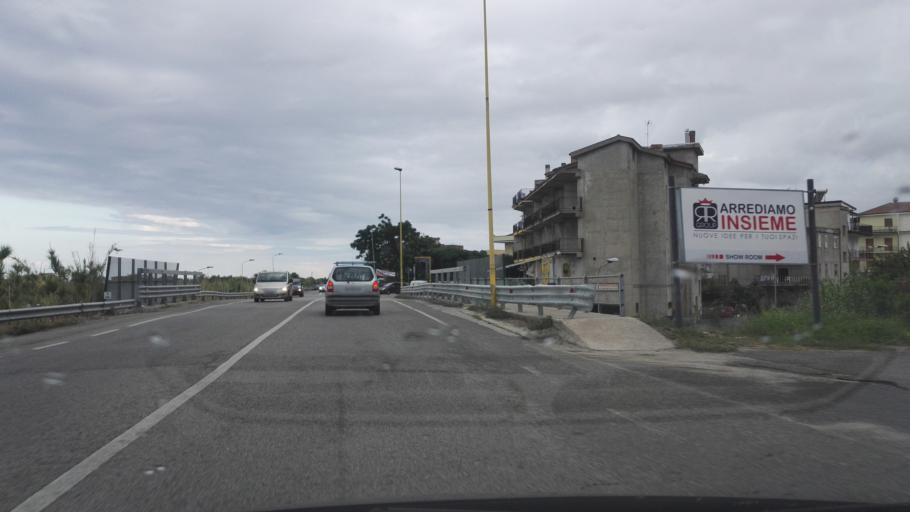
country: IT
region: Calabria
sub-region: Provincia di Catanzaro
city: Isca Marina
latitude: 38.6063
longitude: 16.5564
